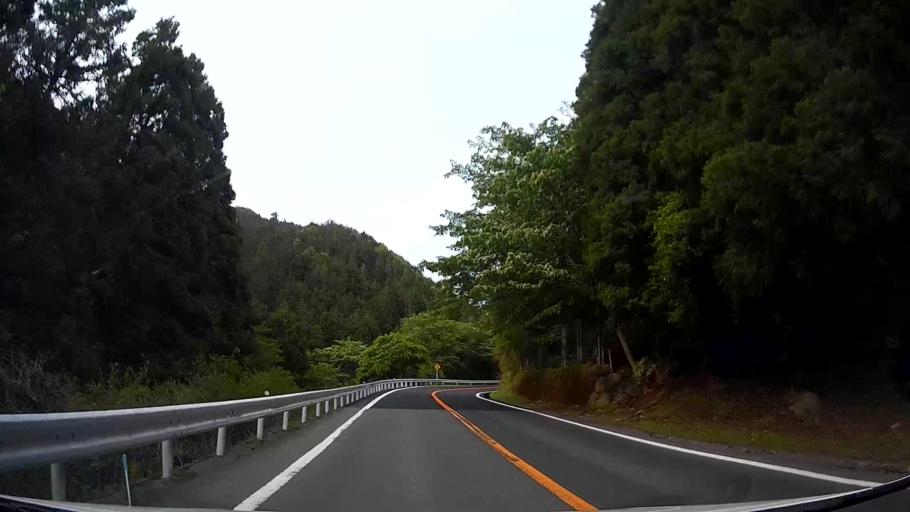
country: JP
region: Shizuoka
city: Ito
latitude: 34.9771
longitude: 139.0524
